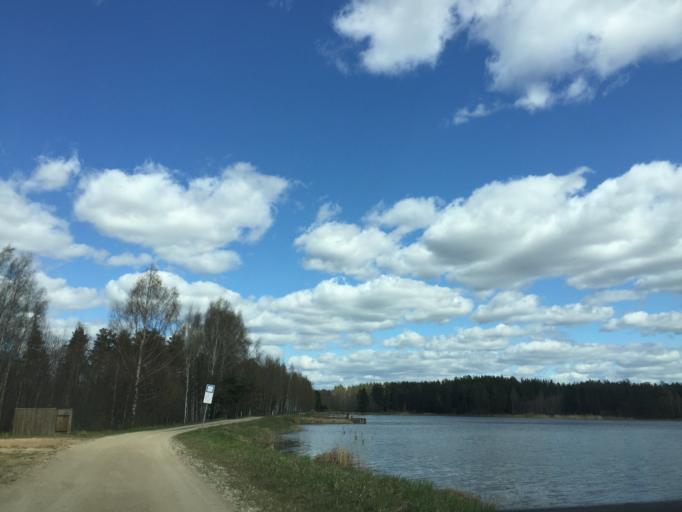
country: LV
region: Rezekne
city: Rezekne
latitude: 56.5712
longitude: 27.1461
